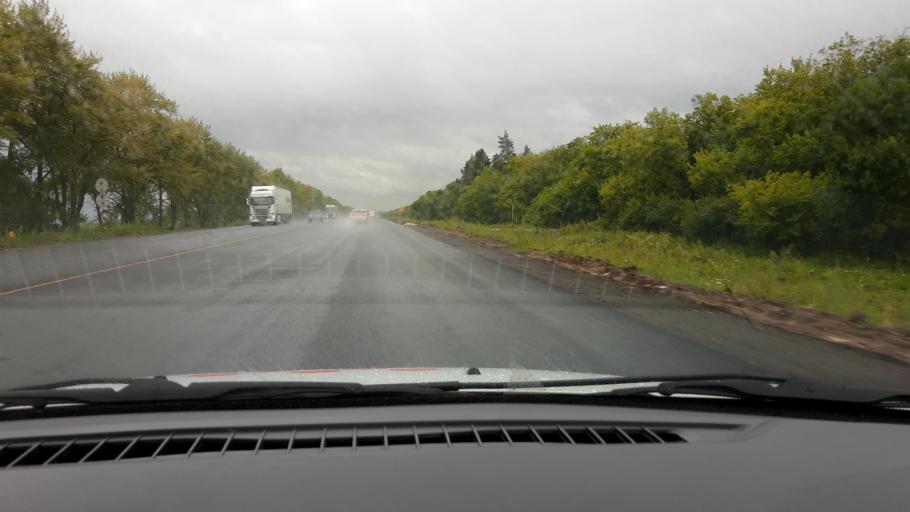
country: RU
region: Chuvashia
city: Yantikovo
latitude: 55.8006
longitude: 47.8703
